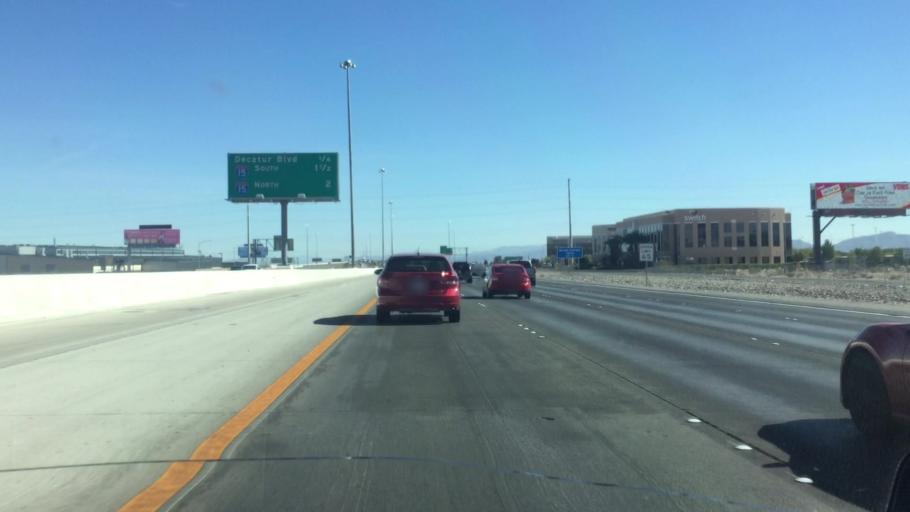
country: US
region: Nevada
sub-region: Clark County
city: Enterprise
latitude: 36.0672
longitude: -115.2168
